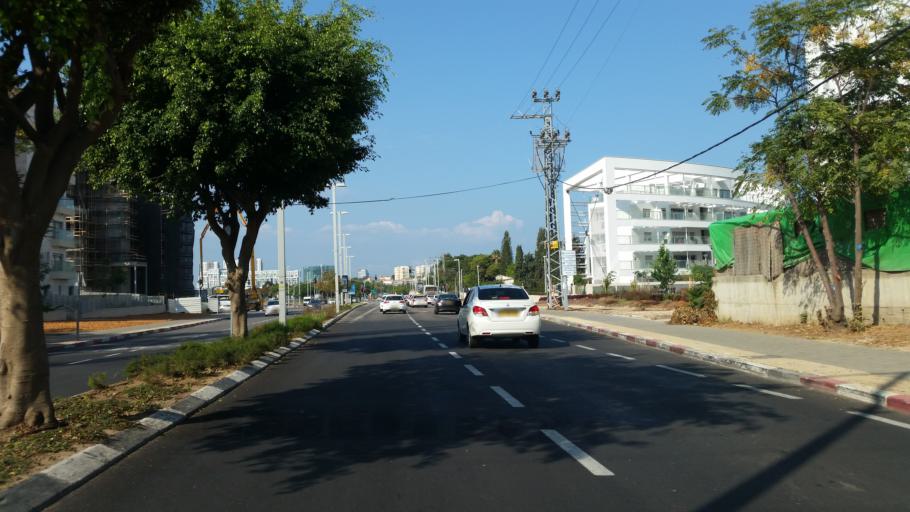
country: IL
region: Tel Aviv
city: Herzliyya
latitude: 32.1632
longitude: 34.8291
